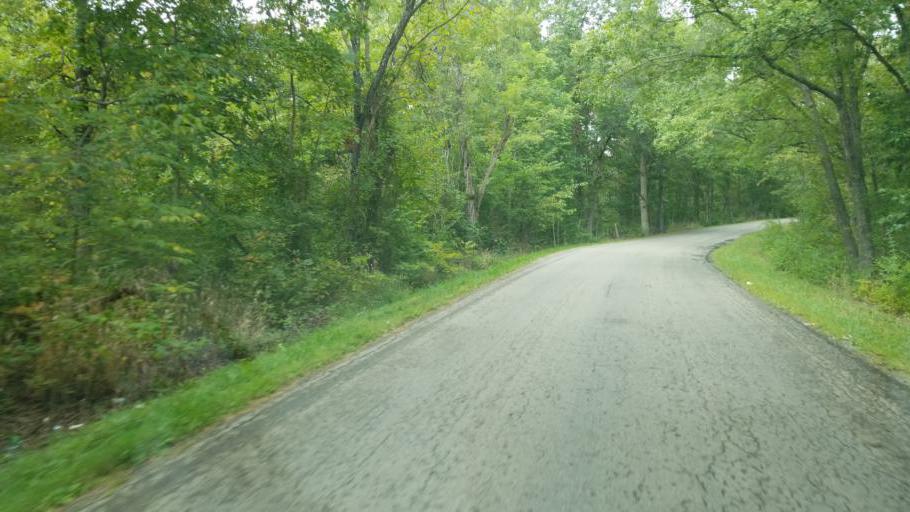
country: US
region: Ohio
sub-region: Jackson County
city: Oak Hill
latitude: 38.8915
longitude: -82.6056
